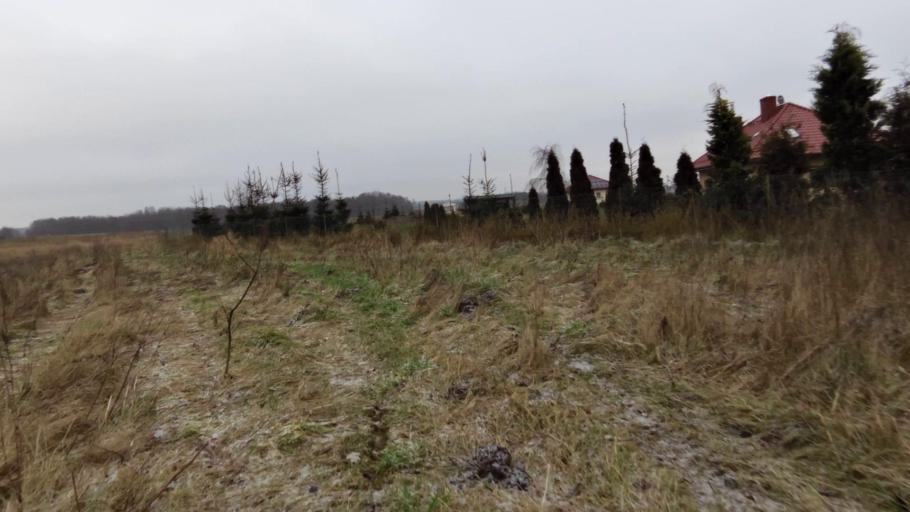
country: PL
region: West Pomeranian Voivodeship
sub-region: Powiat szczecinecki
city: Borne Sulinowo
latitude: 53.6399
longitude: 16.6156
